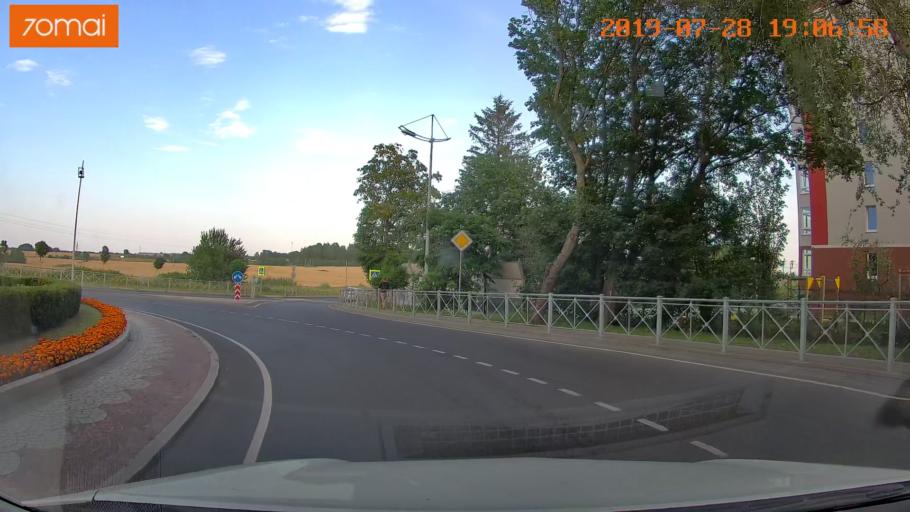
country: RU
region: Kaliningrad
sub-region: Gorod Svetlogorsk
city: Svetlogorsk
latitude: 54.9293
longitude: 20.1680
